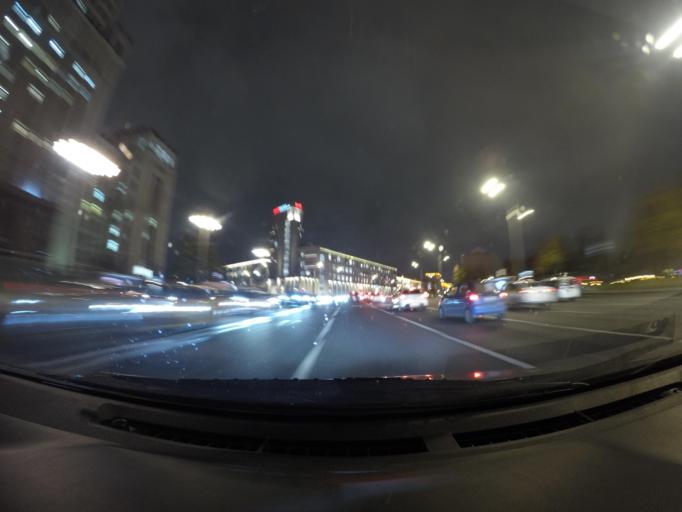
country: RU
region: Moscow
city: Moscow
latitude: 55.7688
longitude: 37.6486
